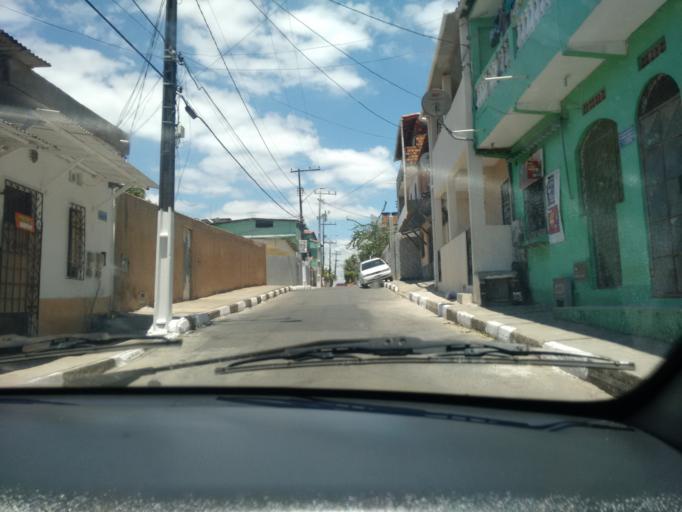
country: BR
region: Bahia
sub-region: Lauro De Freitas
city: Lauro de Freitas
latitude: -12.8943
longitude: -38.3364
